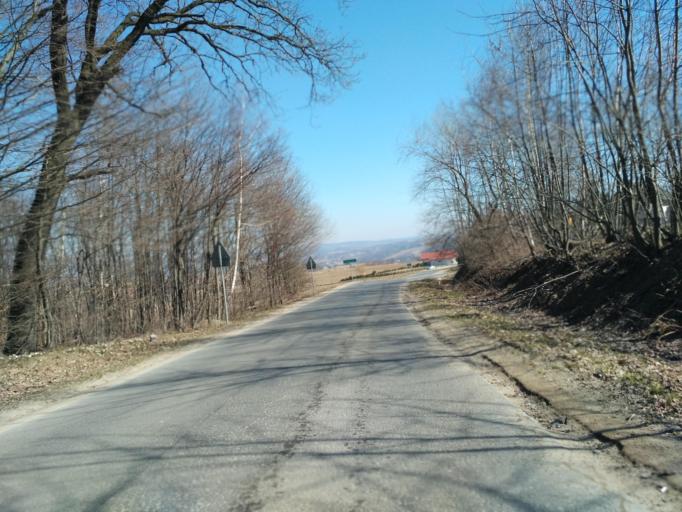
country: PL
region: Subcarpathian Voivodeship
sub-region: Powiat ropczycko-sedziszowski
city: Niedzwiada
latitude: 49.9661
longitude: 21.4667
